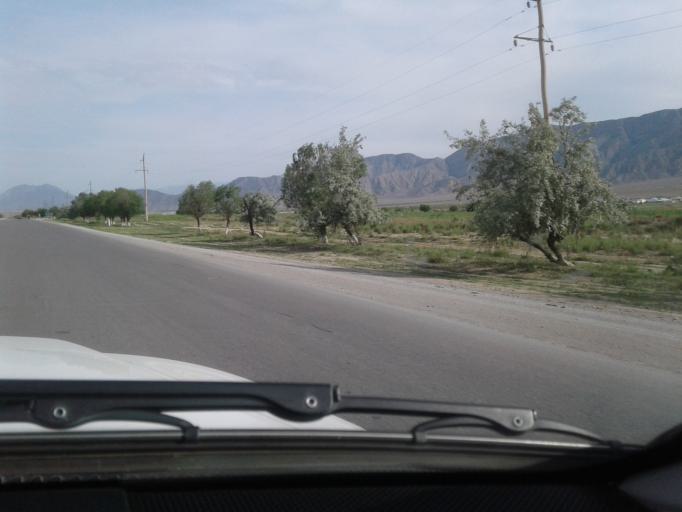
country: TM
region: Ahal
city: Arcabil
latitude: 38.1948
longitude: 57.8354
